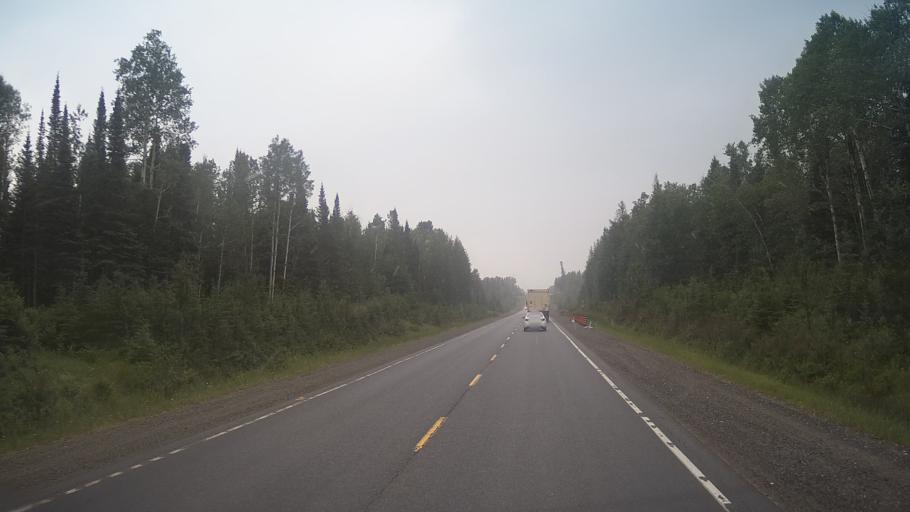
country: CA
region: Ontario
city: Greenstone
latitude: 49.1860
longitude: -88.2201
